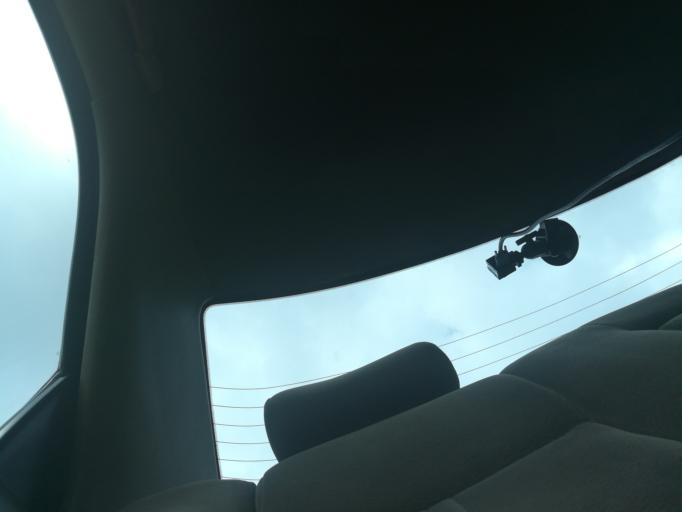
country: NG
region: Lagos
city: Ikorodu
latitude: 6.6552
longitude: 3.5813
